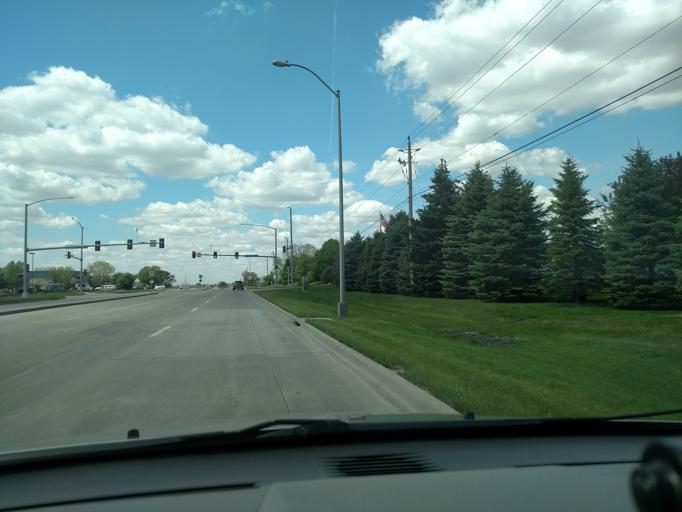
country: US
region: Iowa
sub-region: Polk County
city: Ankeny
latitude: 41.7029
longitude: -93.5929
